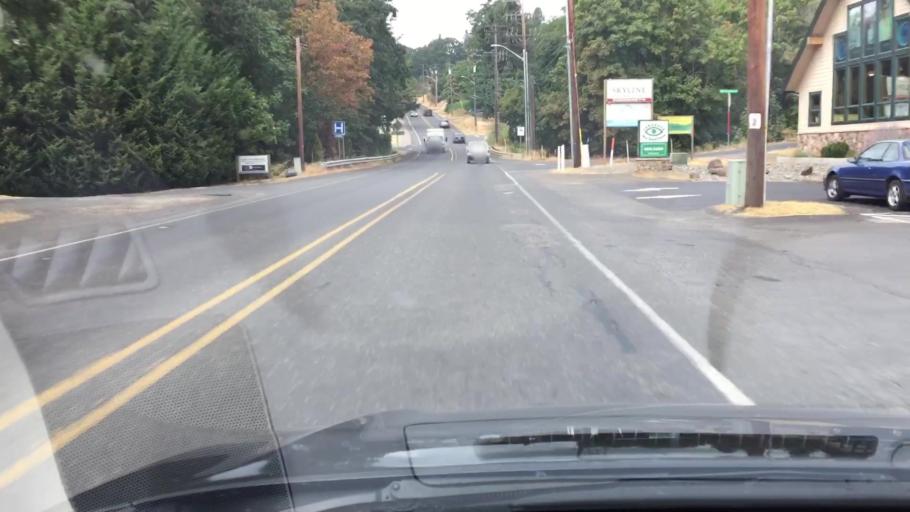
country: US
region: Washington
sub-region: Klickitat County
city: White Salmon
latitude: 45.7218
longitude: -121.4729
